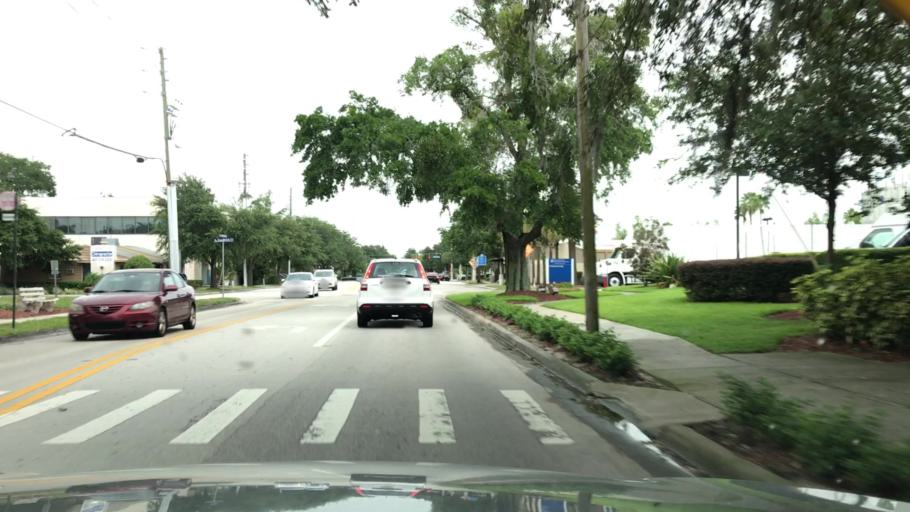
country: US
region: Florida
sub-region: Orange County
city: Winter Park
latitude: 28.5983
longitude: -81.3279
